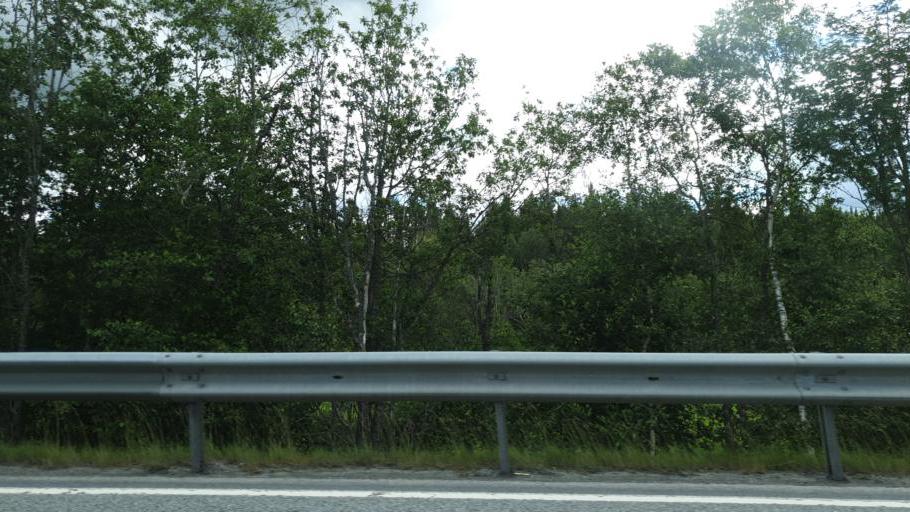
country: NO
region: Sor-Trondelag
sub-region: Rennebu
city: Berkak
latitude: 62.8766
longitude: 10.0880
